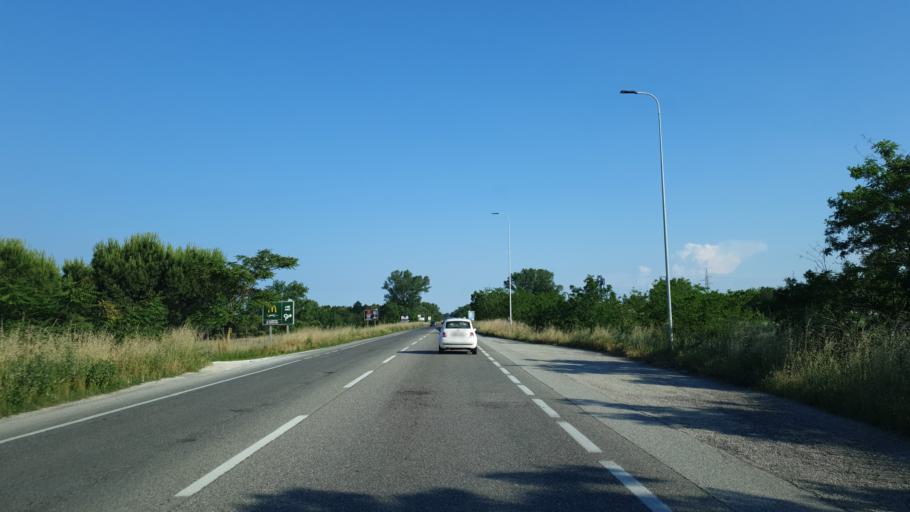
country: IT
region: Emilia-Romagna
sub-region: Provincia di Ravenna
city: Fosso Ghiaia
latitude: 44.3453
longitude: 12.2631
